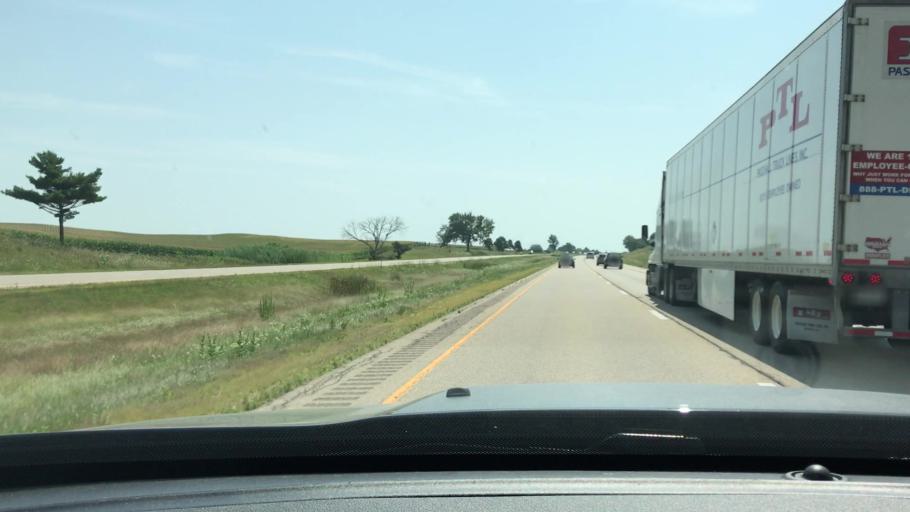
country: US
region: Illinois
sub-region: Bureau County
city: Ladd
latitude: 41.3866
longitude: -89.2764
